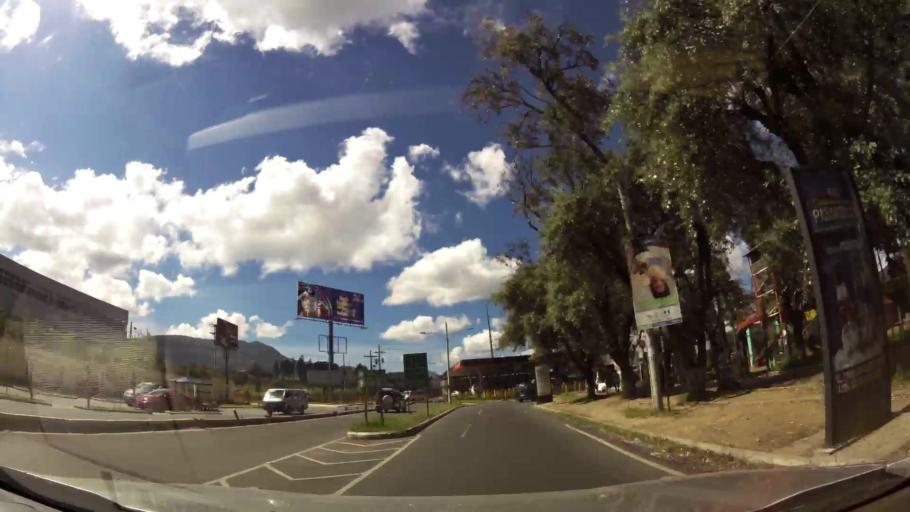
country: GT
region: Quetzaltenango
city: Quetzaltenango
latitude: 14.8464
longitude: -91.5360
